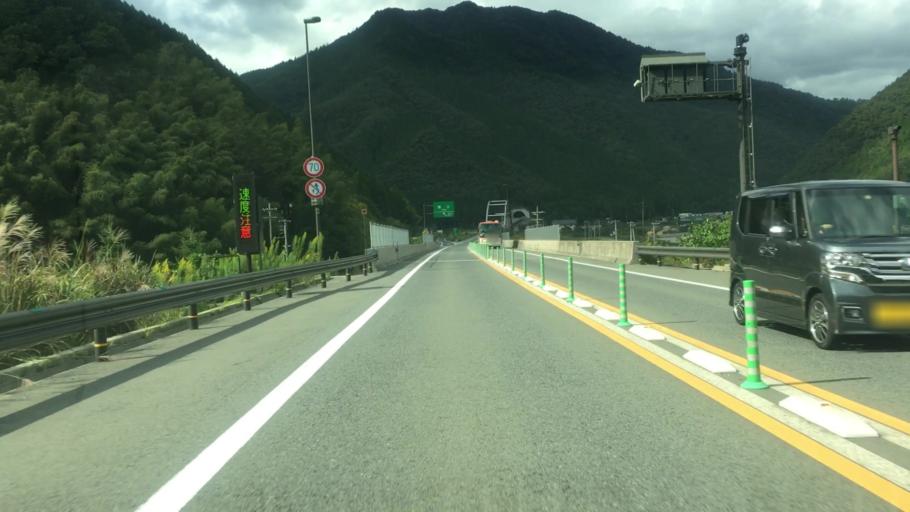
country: JP
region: Hyogo
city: Toyooka
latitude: 35.3559
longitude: 134.7643
